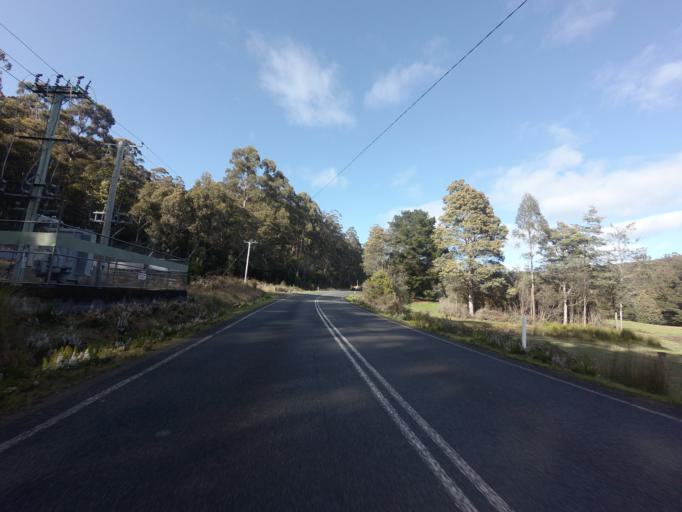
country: AU
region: Tasmania
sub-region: Huon Valley
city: Cygnet
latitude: -43.2734
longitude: 147.0105
